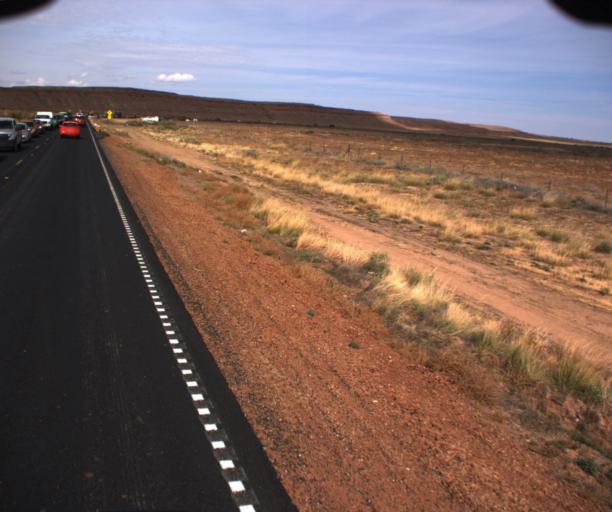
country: US
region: Arizona
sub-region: Apache County
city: Chinle
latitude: 36.1117
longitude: -109.6360
